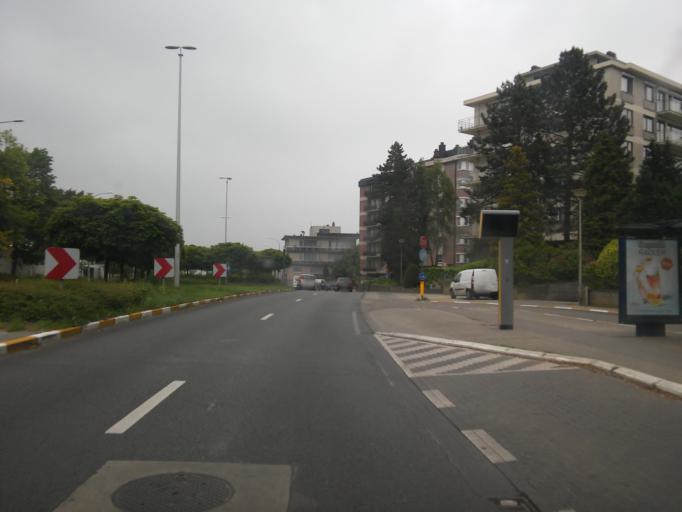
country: BE
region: Flanders
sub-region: Provincie Vlaams-Brabant
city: Dilbeek
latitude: 50.8433
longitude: 4.2566
